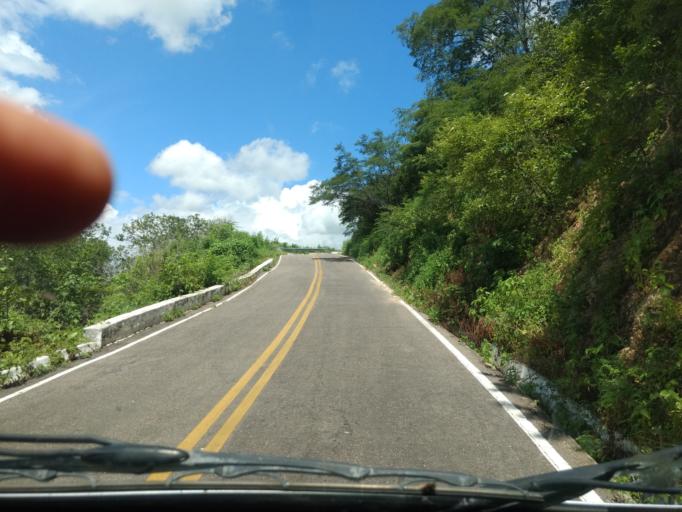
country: BR
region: Ceara
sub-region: Crateus
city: Crateus
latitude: -5.2410
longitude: -40.8982
